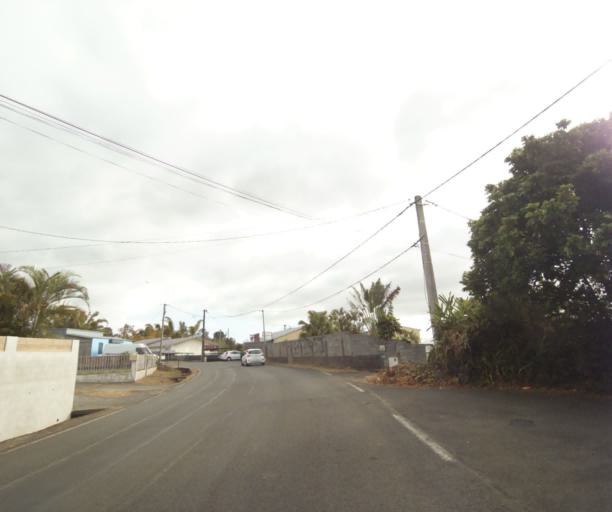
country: RE
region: Reunion
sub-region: Reunion
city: Saint-Paul
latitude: -21.0387
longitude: 55.3056
